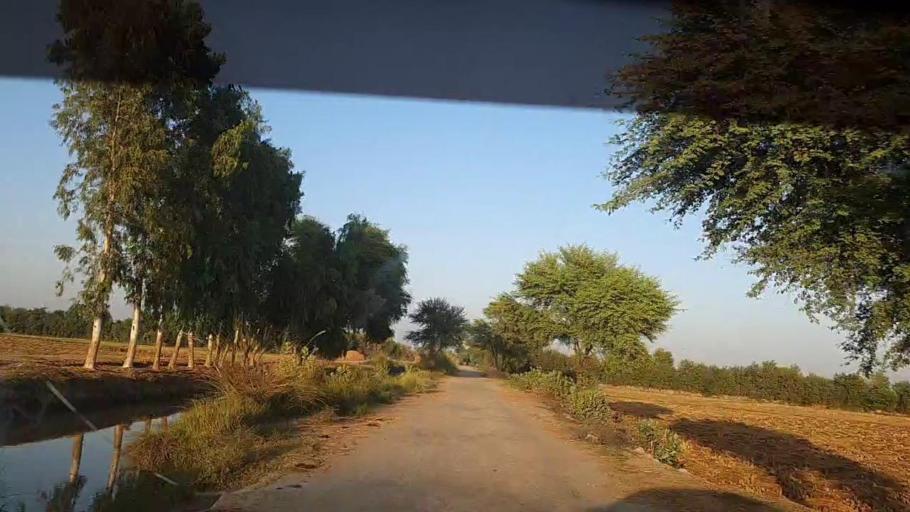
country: PK
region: Sindh
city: Ratodero
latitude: 27.8796
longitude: 68.2043
